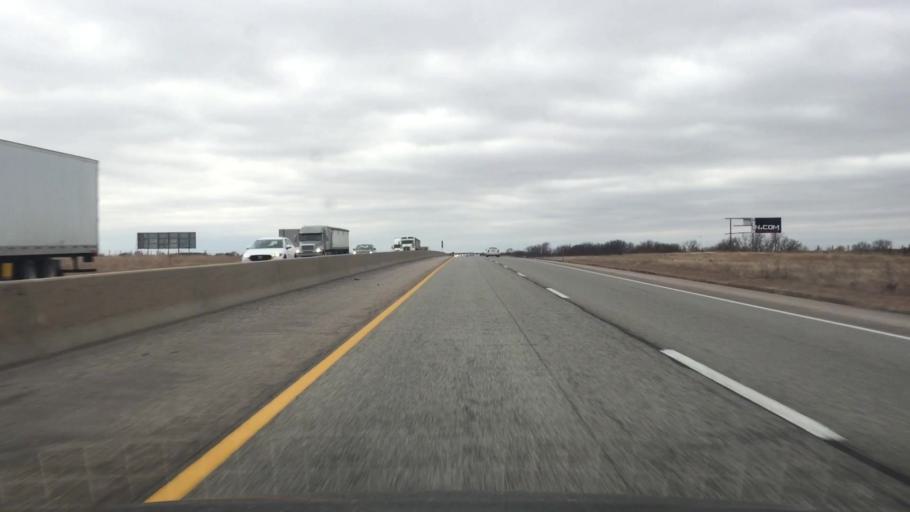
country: US
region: Kansas
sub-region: Butler County
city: El Dorado
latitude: 38.0275
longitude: -96.6613
